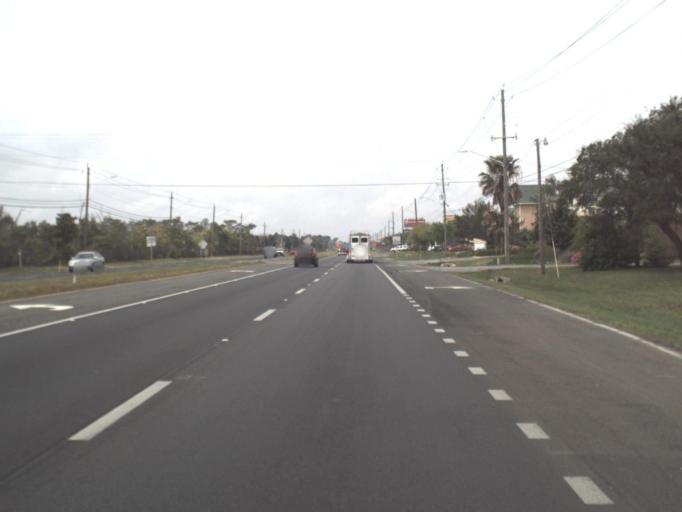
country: US
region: Florida
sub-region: Santa Rosa County
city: Navarre
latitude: 30.4019
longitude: -86.8962
